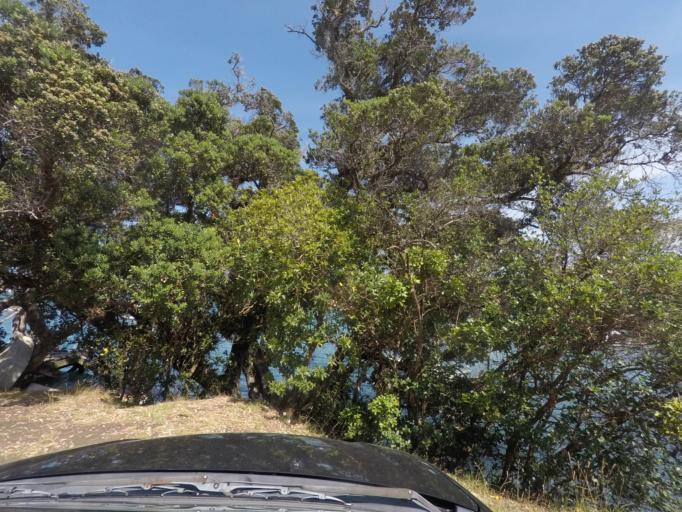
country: NZ
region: Auckland
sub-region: Auckland
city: Warkworth
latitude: -36.3176
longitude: 174.7847
